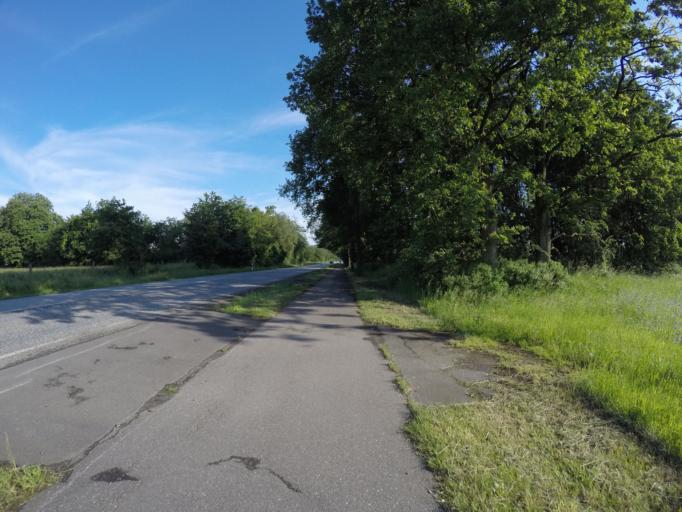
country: DE
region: Schleswig-Holstein
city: Lentfohrden
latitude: 53.8647
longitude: 9.8885
